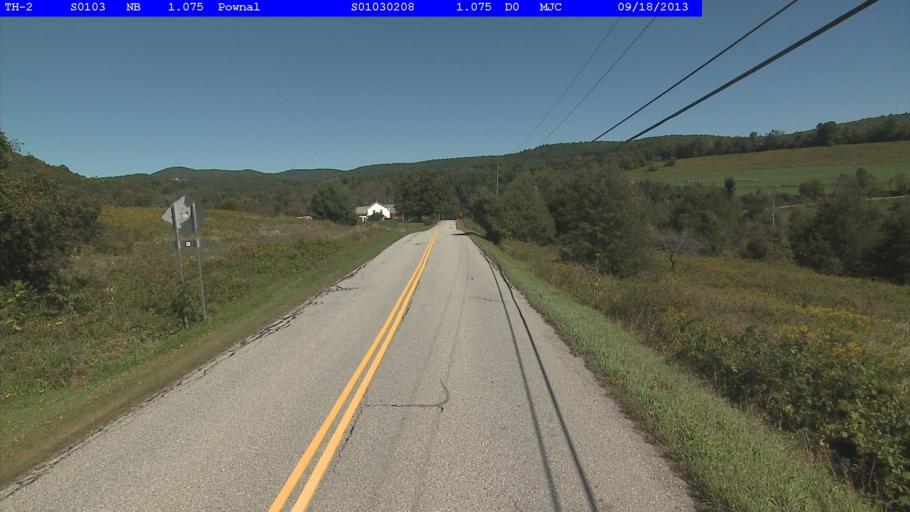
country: US
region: Vermont
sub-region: Bennington County
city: Bennington
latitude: 42.8023
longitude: -73.2495
